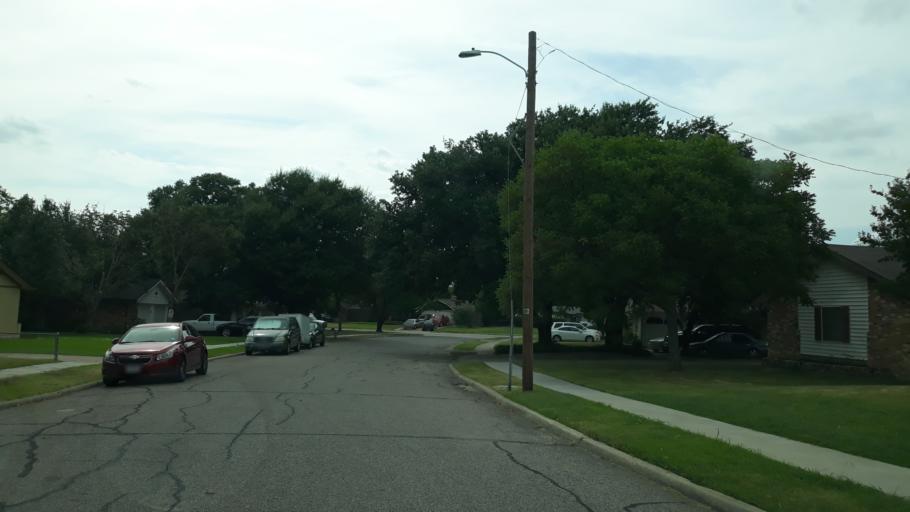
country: US
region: Texas
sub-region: Dallas County
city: Irving
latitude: 32.8515
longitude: -96.9853
